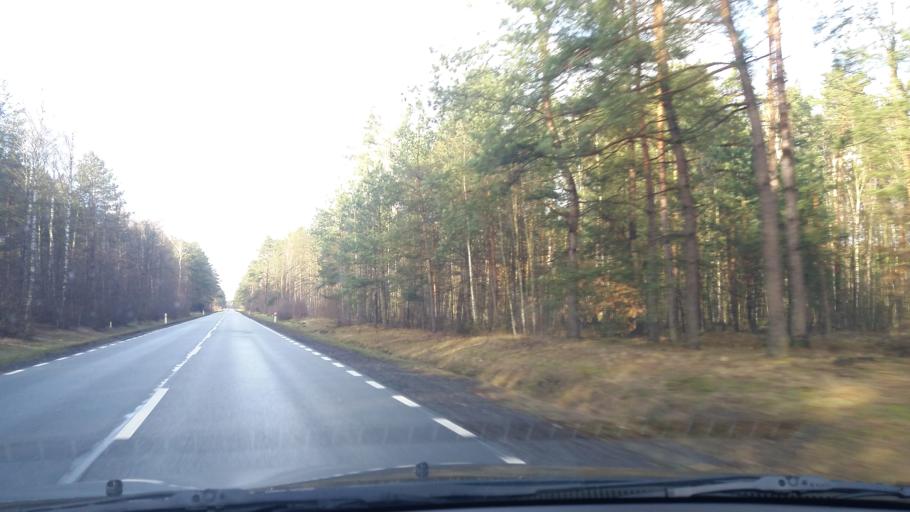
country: PL
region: Masovian Voivodeship
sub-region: Powiat przasnyski
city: Chorzele
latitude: 53.2986
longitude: 20.9141
